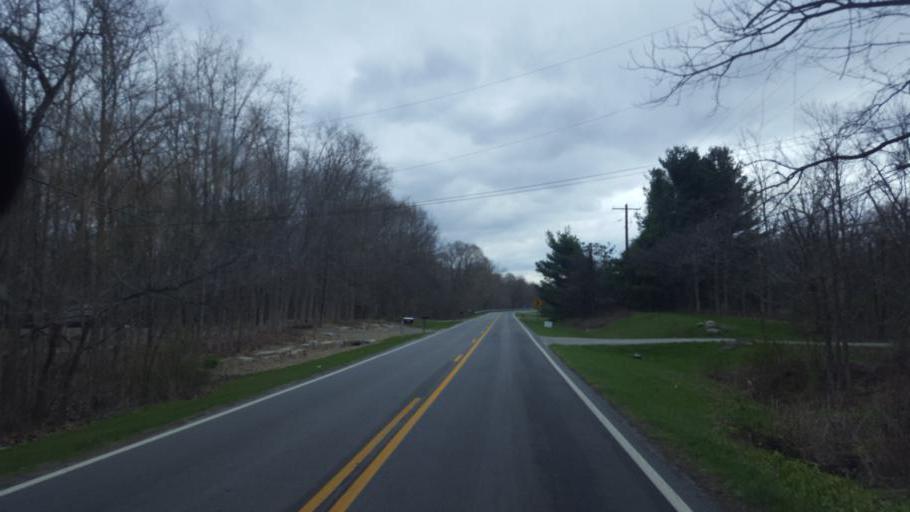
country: US
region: Ohio
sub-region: Delaware County
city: Sunbury
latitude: 40.1874
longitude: -82.8716
